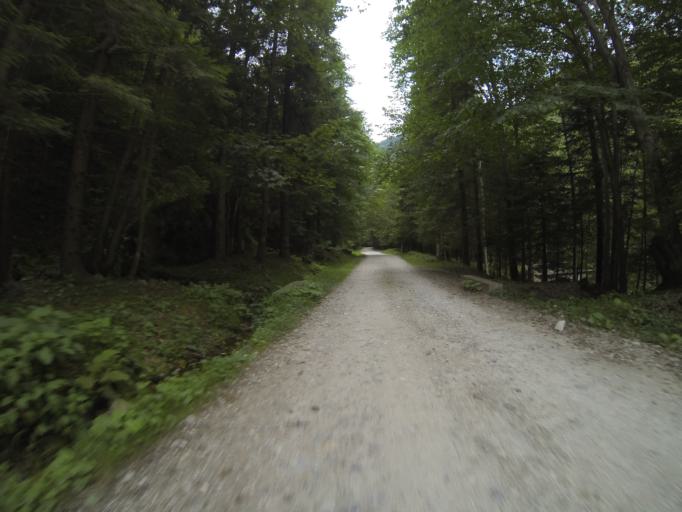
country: RO
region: Gorj
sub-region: Comuna Polovragi
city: Polovragi
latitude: 45.2554
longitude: 23.7687
